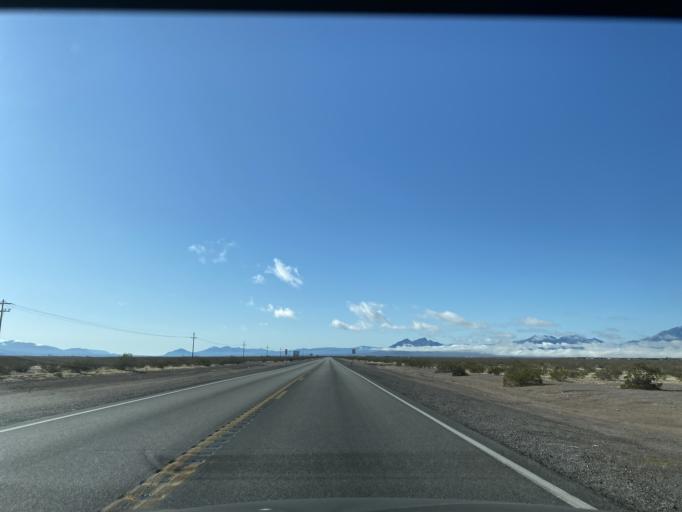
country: US
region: Nevada
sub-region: Nye County
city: Beatty
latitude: 36.5692
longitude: -116.4136
